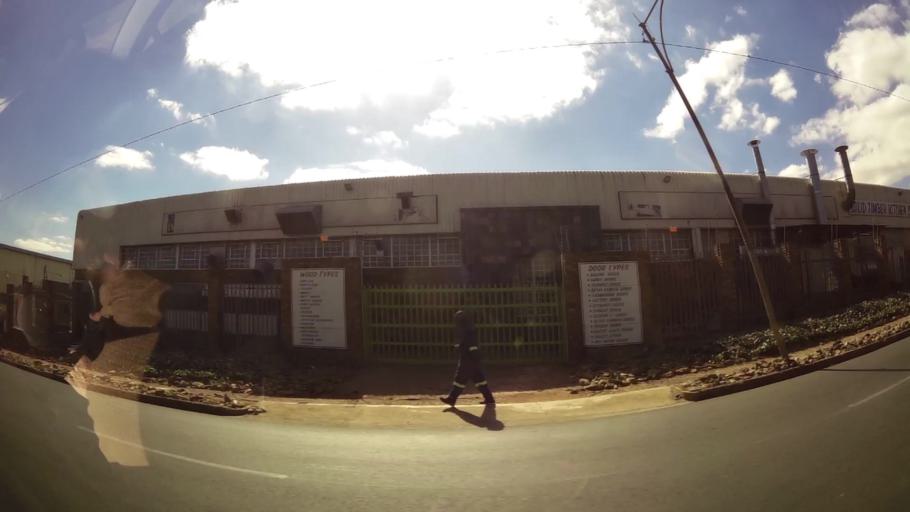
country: ZA
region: Gauteng
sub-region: West Rand District Municipality
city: Krugersdorp
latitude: -26.1184
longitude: 27.8065
